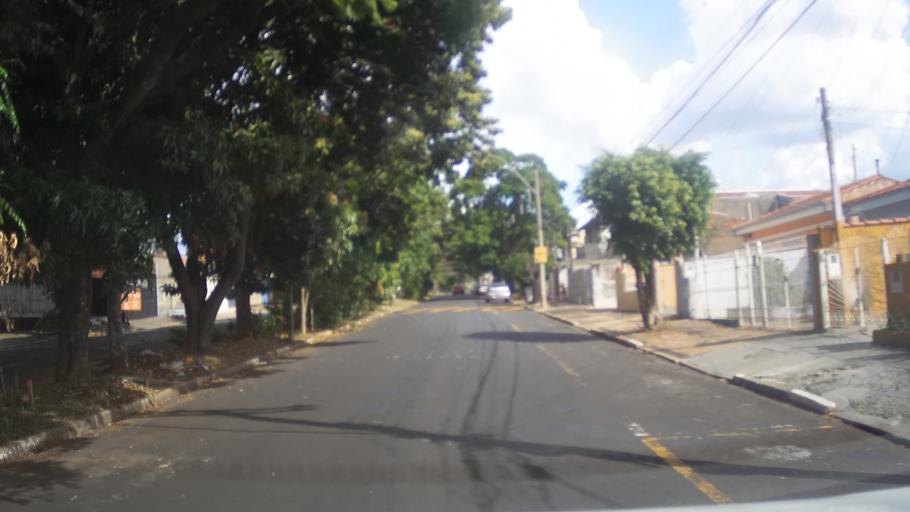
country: BR
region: Sao Paulo
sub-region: Campinas
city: Campinas
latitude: -22.8881
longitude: -47.1087
